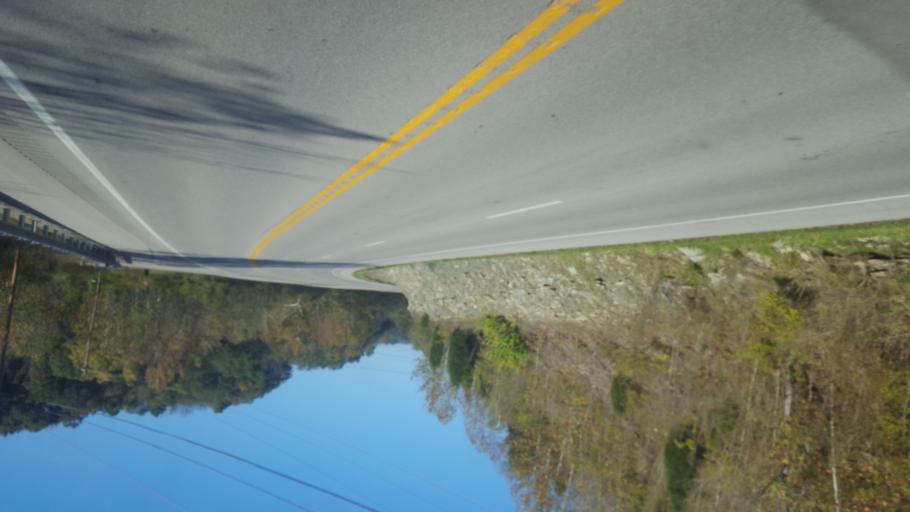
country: US
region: Kentucky
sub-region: Mason County
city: Maysville
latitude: 38.6175
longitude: -83.7532
